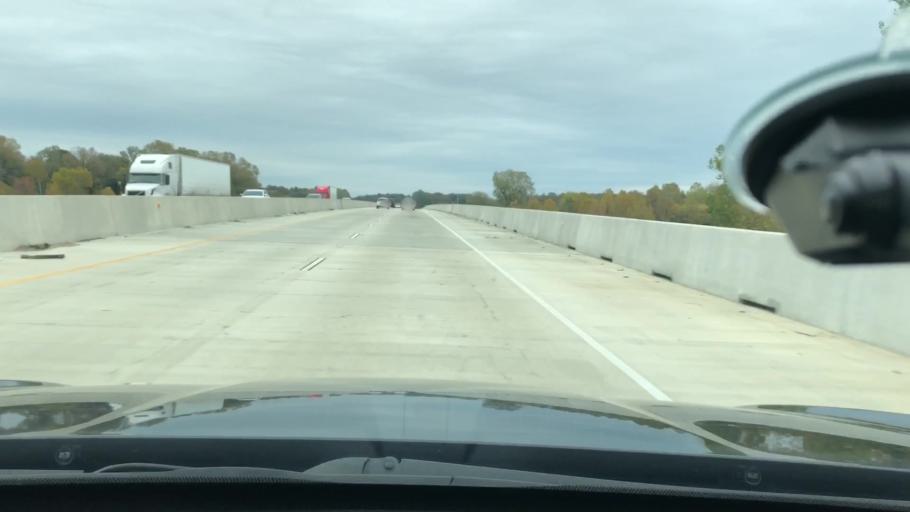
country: US
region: Arkansas
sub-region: Hempstead County
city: Hope
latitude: 33.6051
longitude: -93.8150
